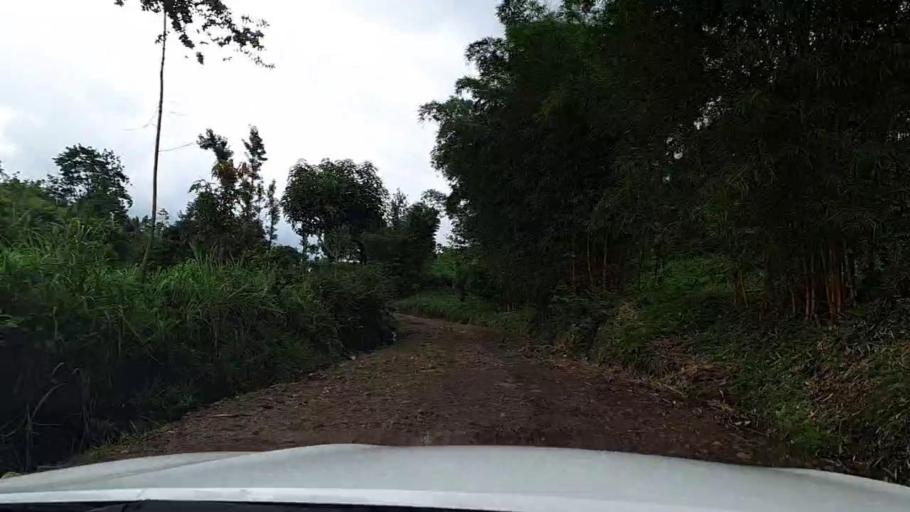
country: RW
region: Western Province
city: Cyangugu
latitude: -2.5626
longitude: 29.0361
